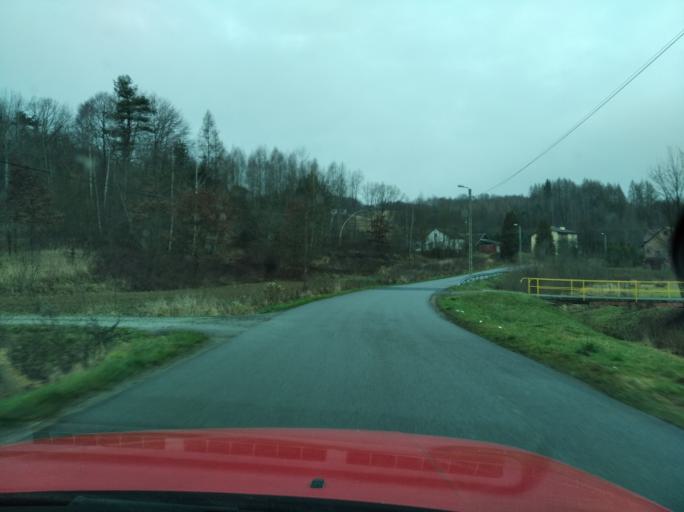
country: PL
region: Subcarpathian Voivodeship
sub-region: Powiat przemyski
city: Nienadowa
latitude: 49.8522
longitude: 22.4237
